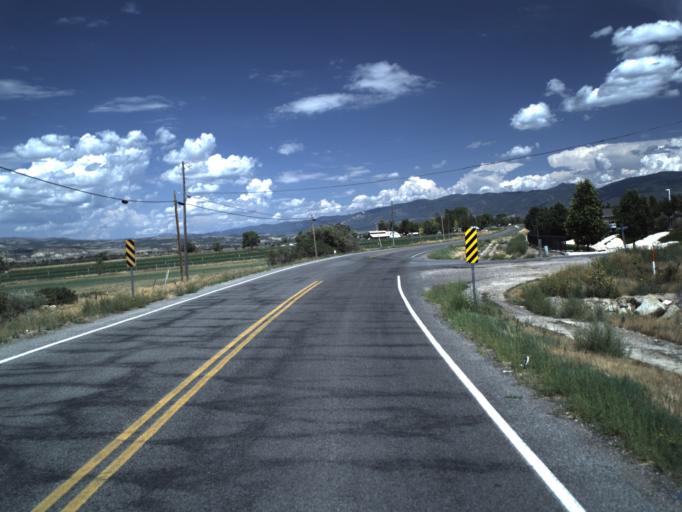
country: US
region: Utah
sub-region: Sanpete County
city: Mount Pleasant
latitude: 39.4911
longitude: -111.4957
